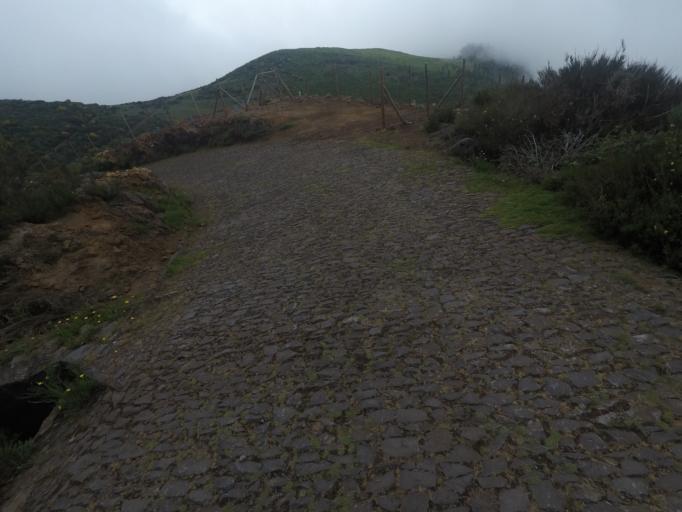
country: PT
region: Madeira
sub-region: Calheta
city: Arco da Calheta
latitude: 32.7353
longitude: -17.0989
